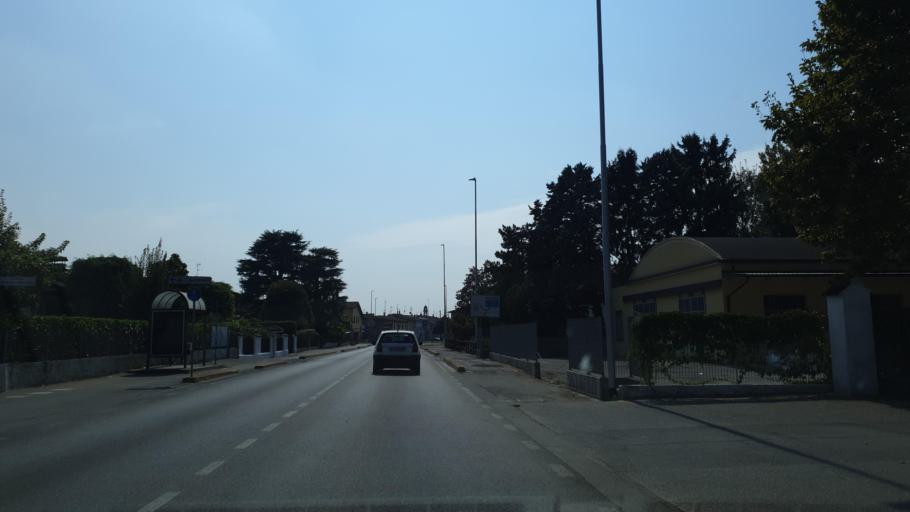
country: IT
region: Lombardy
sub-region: Provincia di Brescia
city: Pralboino
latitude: 45.2721
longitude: 10.2172
